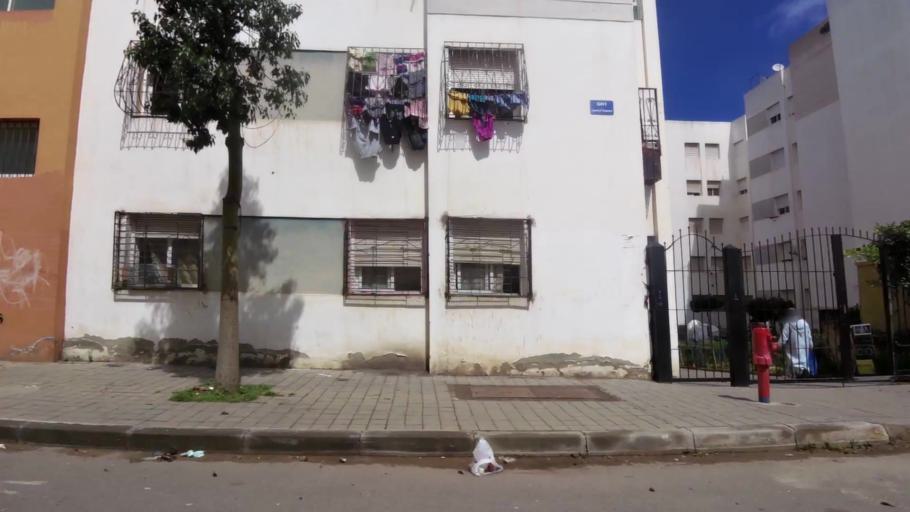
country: MA
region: Grand Casablanca
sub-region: Nouaceur
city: Dar Bouazza
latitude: 33.5358
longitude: -7.7170
